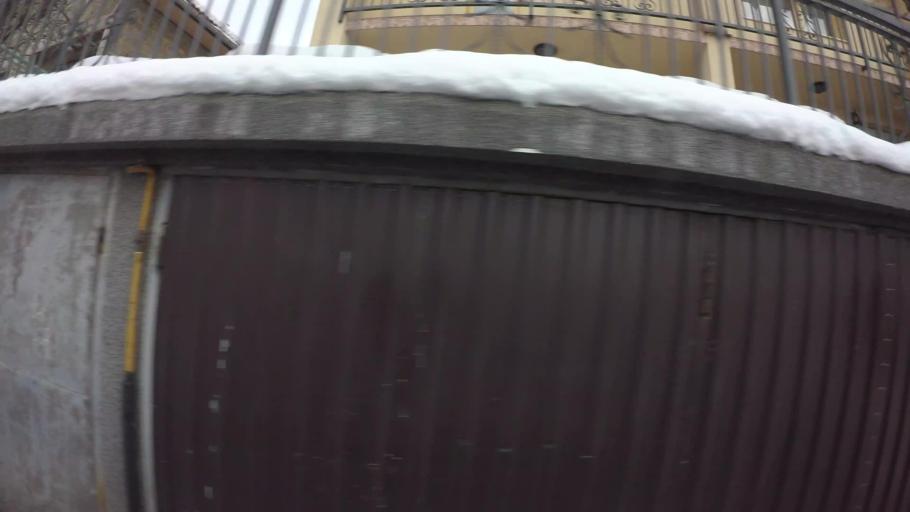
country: BA
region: Federation of Bosnia and Herzegovina
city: Kobilja Glava
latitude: 43.8625
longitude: 18.3779
